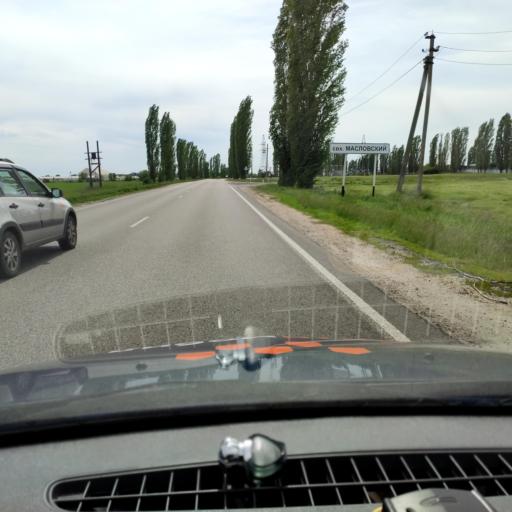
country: RU
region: Voronezj
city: Novaya Usman'
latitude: 51.5464
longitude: 39.3609
